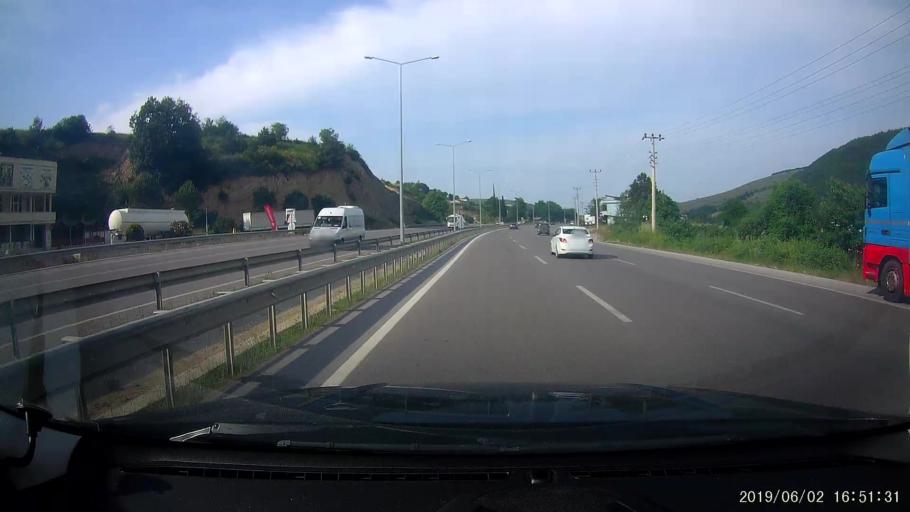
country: TR
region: Samsun
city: Taflan
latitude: 41.2750
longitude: 36.1834
